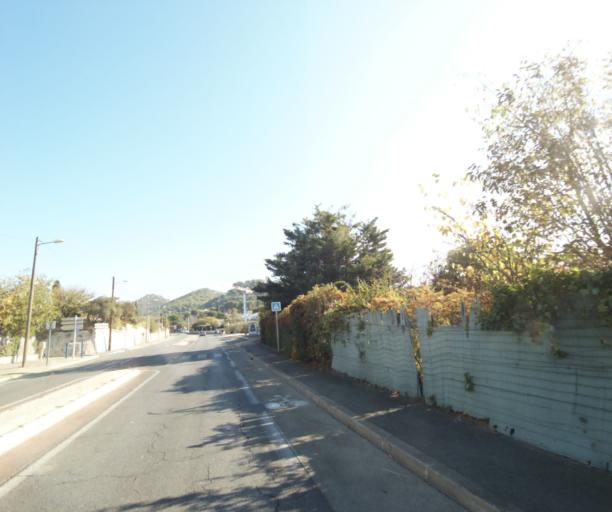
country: FR
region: Provence-Alpes-Cote d'Azur
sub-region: Departement des Bouches-du-Rhone
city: Allauch
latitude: 43.3382
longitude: 5.4762
